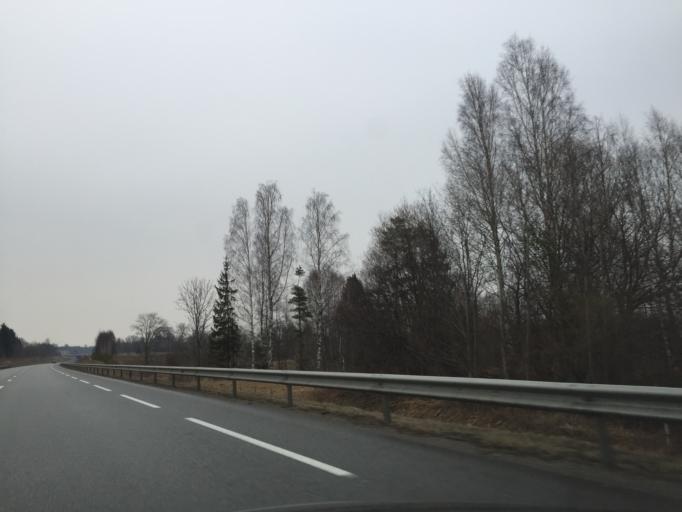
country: LV
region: Saulkrastu
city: Saulkrasti
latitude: 57.3190
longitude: 24.4494
